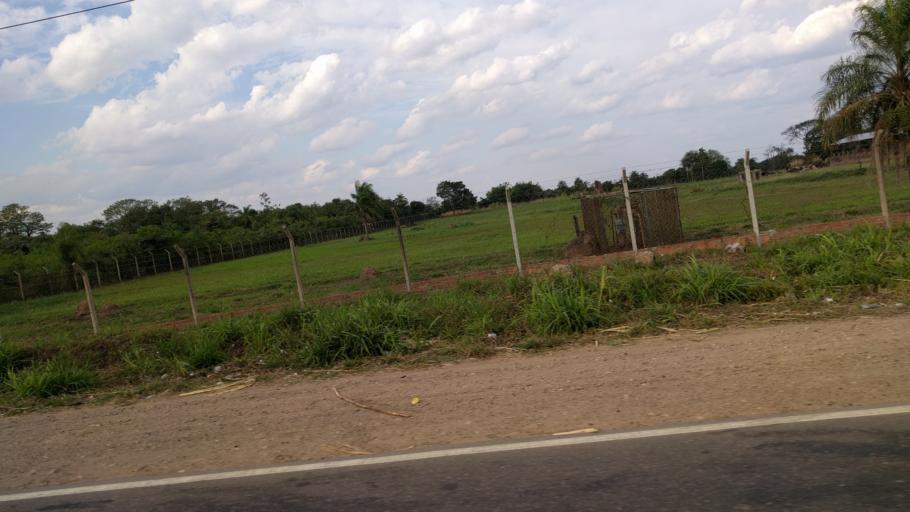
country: BO
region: Santa Cruz
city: Warnes
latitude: -17.5449
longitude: -63.1604
